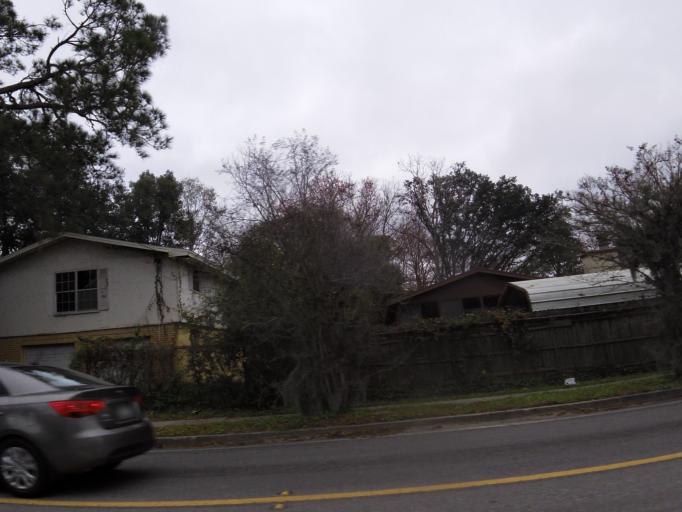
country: US
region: Florida
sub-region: Duval County
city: Jacksonville
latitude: 30.3733
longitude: -81.7130
